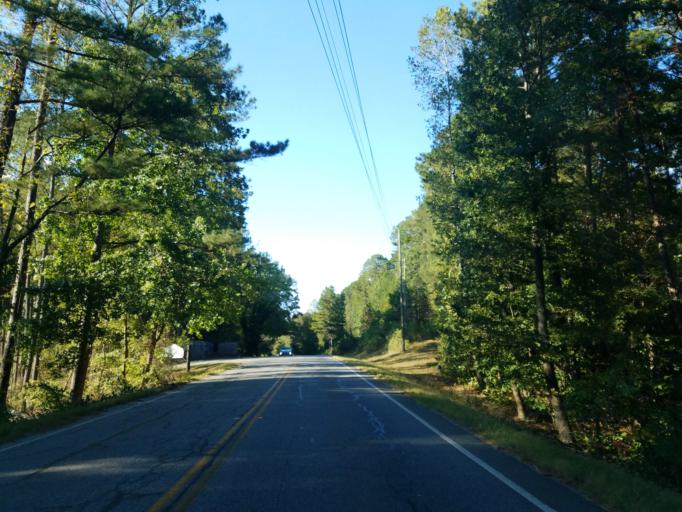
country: US
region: Georgia
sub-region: Bartow County
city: Cartersville
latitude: 34.0898
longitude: -84.8426
